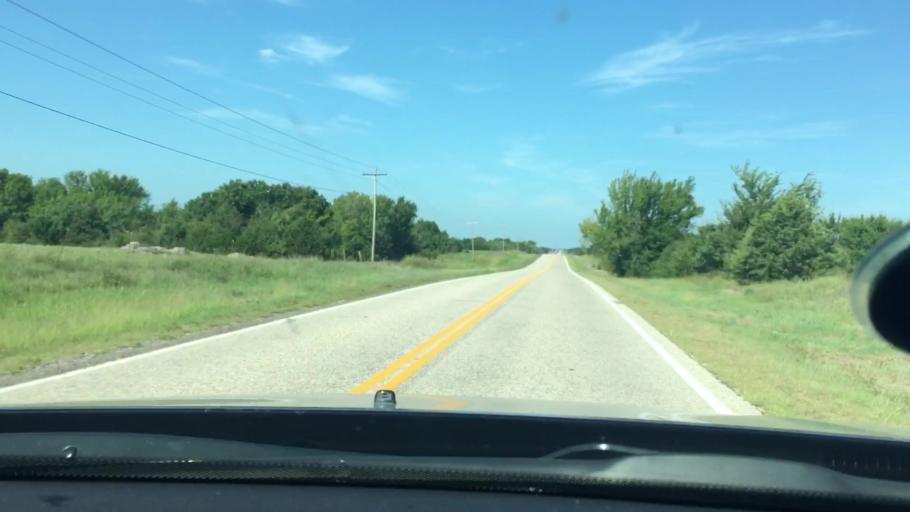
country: US
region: Oklahoma
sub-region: Johnston County
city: Tishomingo
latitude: 34.3614
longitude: -96.5600
